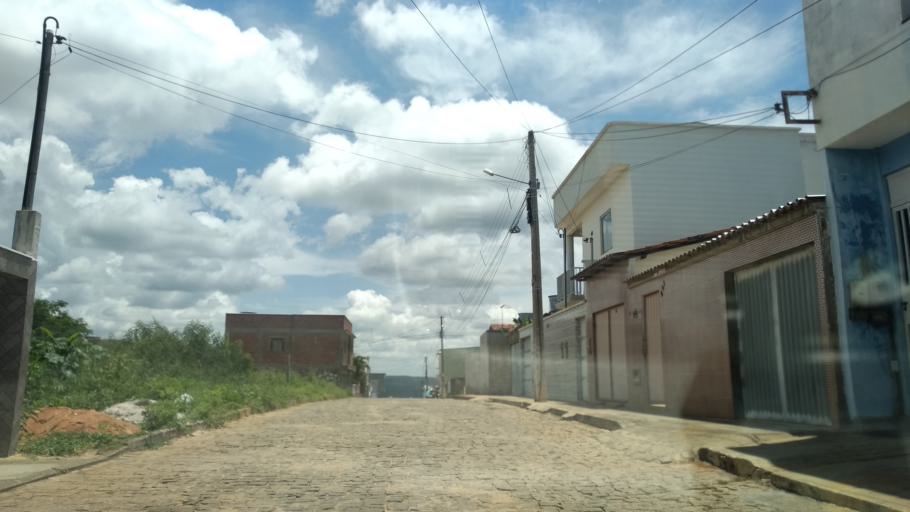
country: BR
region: Bahia
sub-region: Caetite
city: Caetite
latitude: -14.0614
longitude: -42.4881
